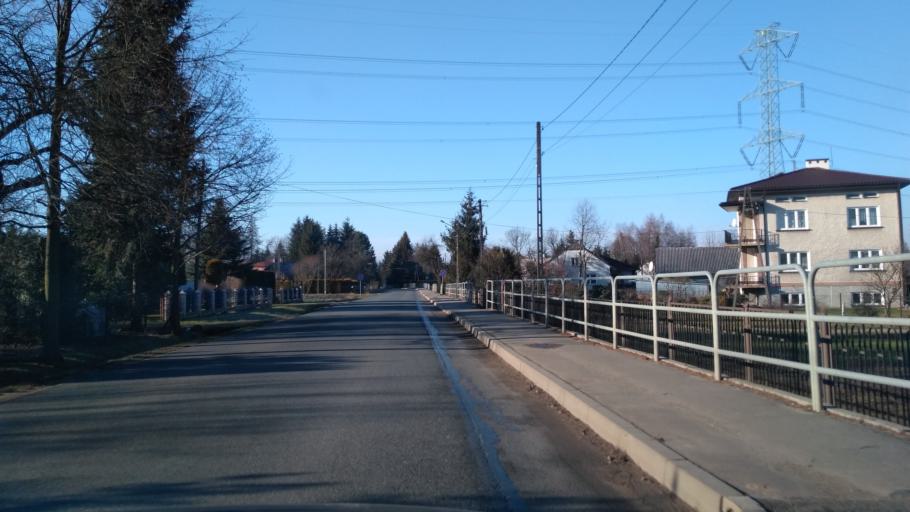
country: PL
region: Subcarpathian Voivodeship
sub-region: Powiat brzozowski
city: Haczow
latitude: 49.6770
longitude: 21.8772
